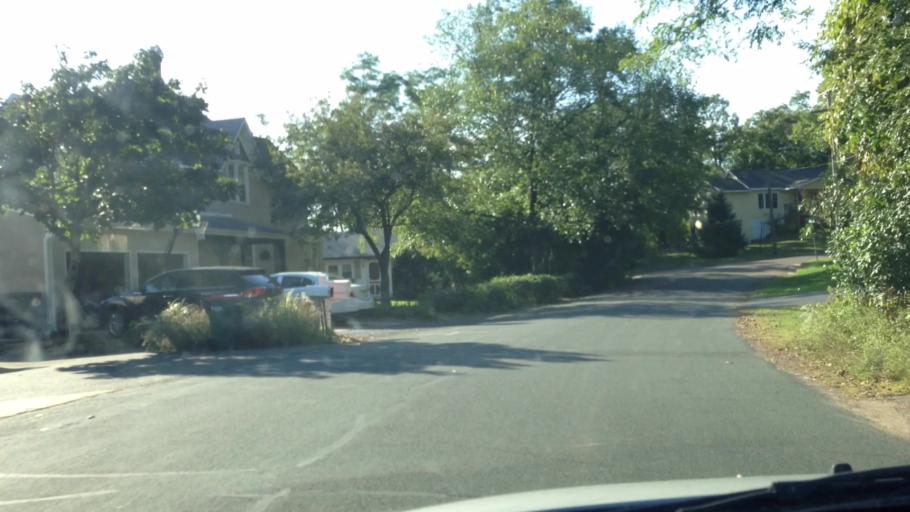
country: US
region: Wisconsin
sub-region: Saint Croix County
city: North Hudson
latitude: 44.9890
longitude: -92.7553
